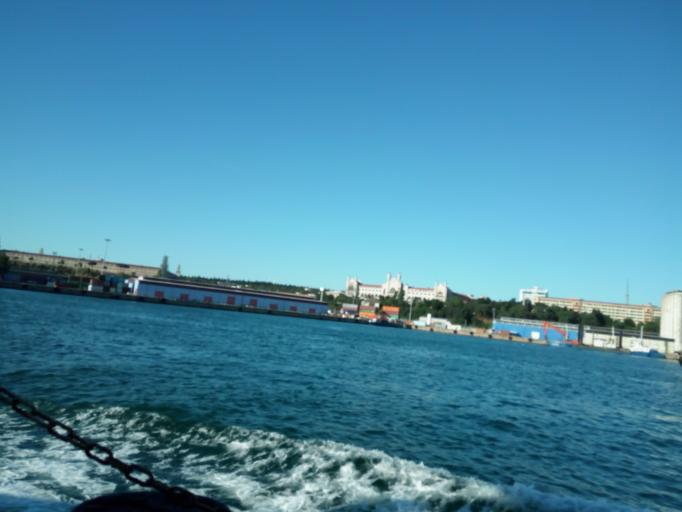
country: TR
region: Istanbul
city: UEskuedar
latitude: 40.9986
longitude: 29.0129
